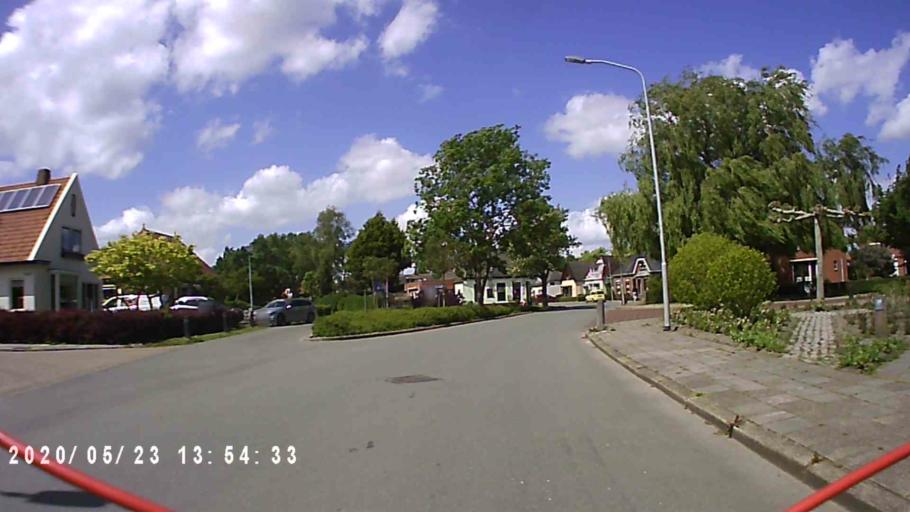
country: NL
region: Groningen
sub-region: Gemeente Delfzijl
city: Delfzijl
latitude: 53.2721
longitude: 7.0310
